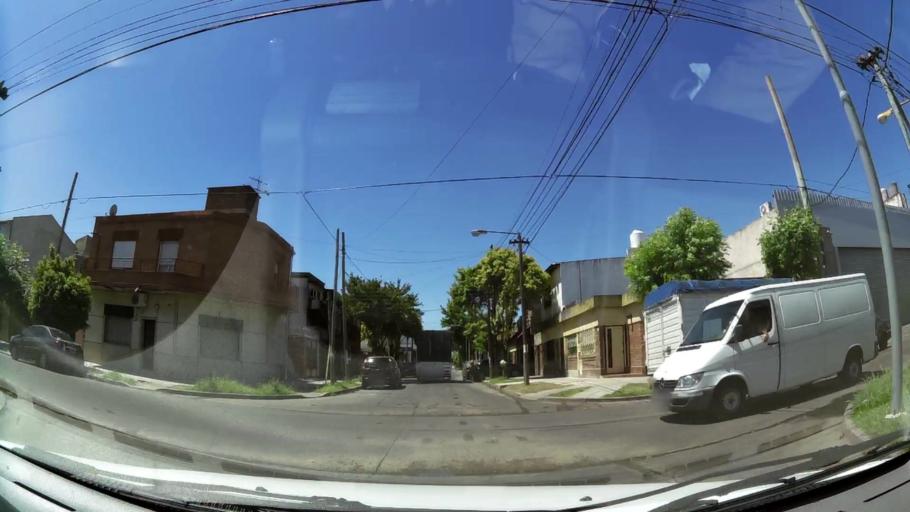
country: AR
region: Buenos Aires
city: Caseros
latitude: -34.5834
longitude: -58.5679
